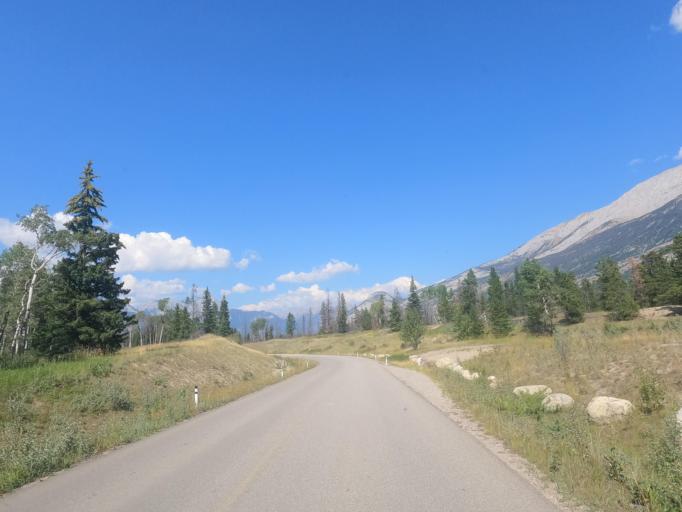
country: CA
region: Alberta
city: Jasper Park Lodge
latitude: 52.9719
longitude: -118.0606
